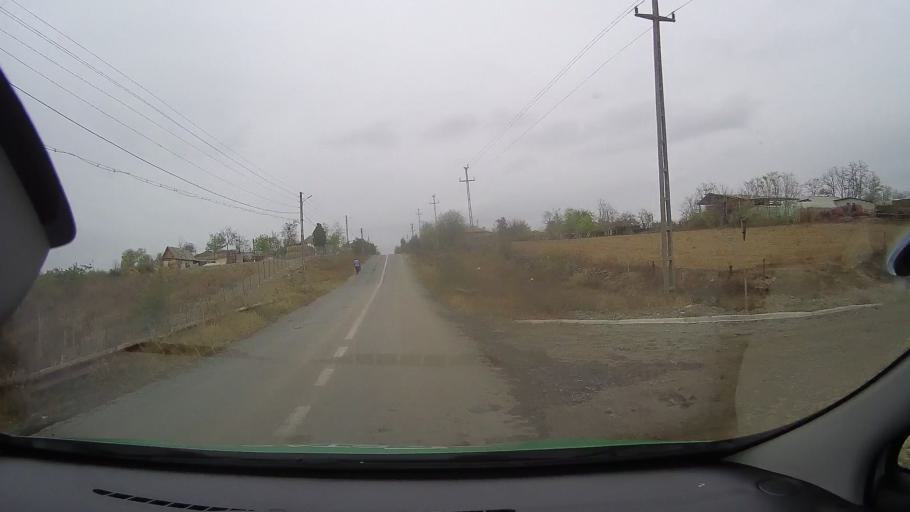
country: RO
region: Constanta
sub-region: Comuna Pantelimon
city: Pantelimon
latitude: 44.5427
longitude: 28.3291
